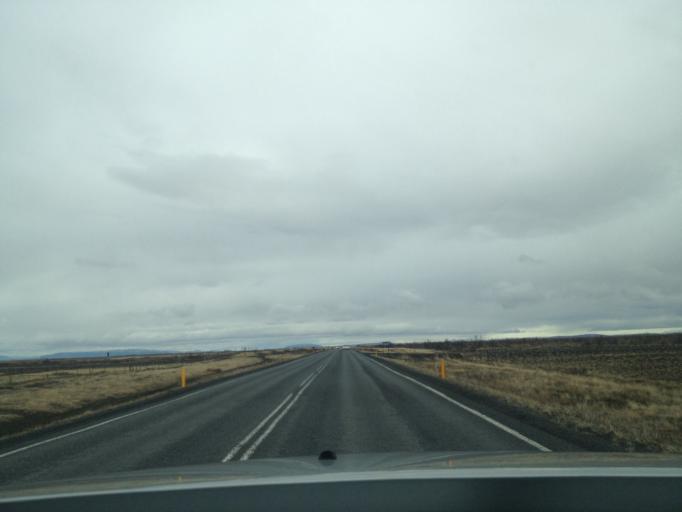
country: IS
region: South
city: Vestmannaeyjar
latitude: 63.8037
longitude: -20.3274
